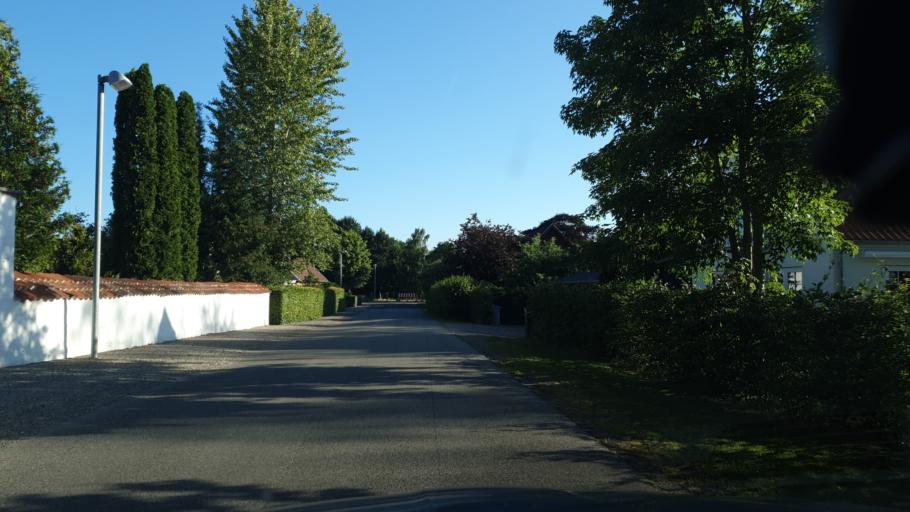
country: DK
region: Zealand
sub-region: Soro Kommune
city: Frederiksberg
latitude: 55.3996
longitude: 11.5653
